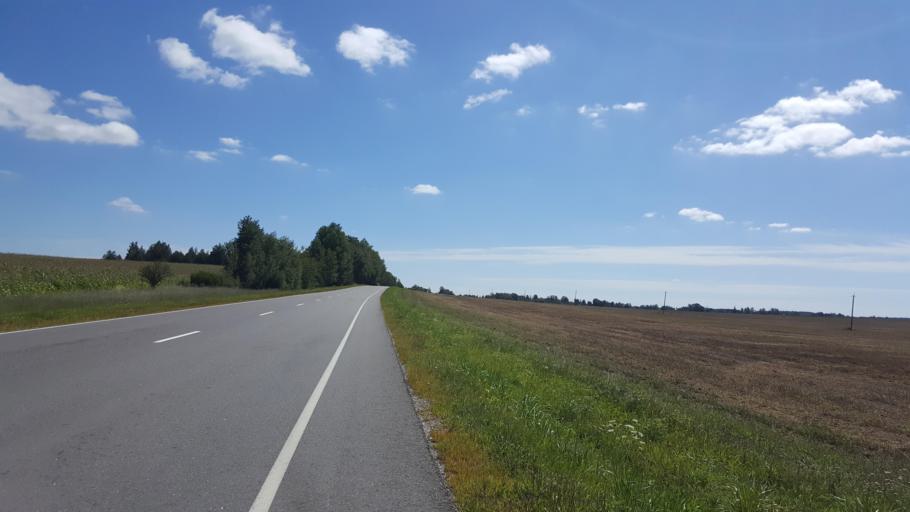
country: BY
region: Brest
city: Zhabinka
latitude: 52.3578
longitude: 24.1676
